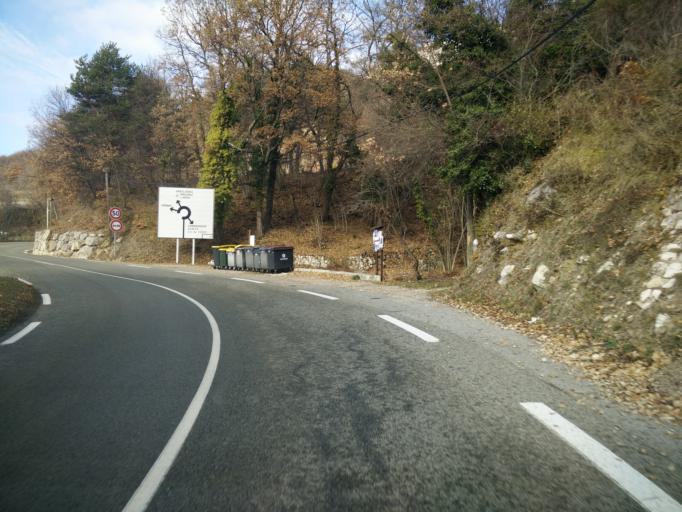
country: FR
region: Provence-Alpes-Cote d'Azur
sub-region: Departement des Alpes-Maritimes
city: Tourrettes-sur-Loup
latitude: 43.7944
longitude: 6.9713
